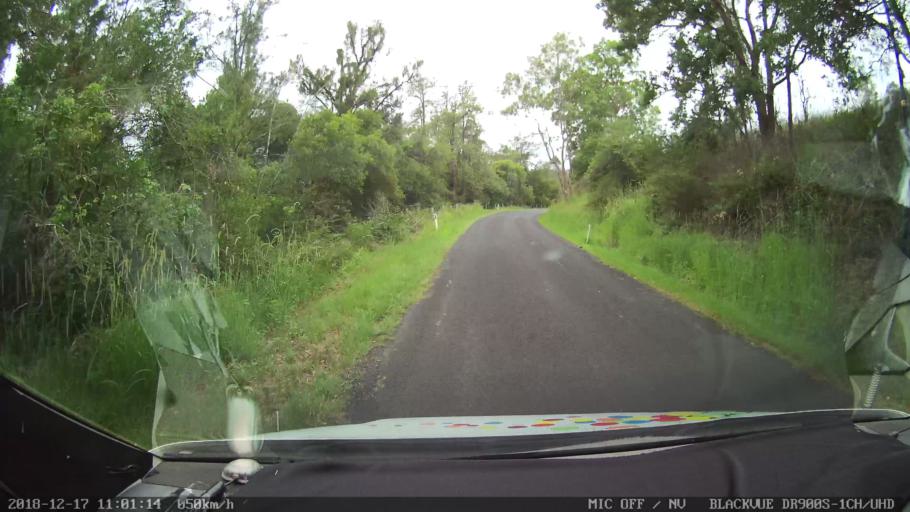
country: AU
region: New South Wales
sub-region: Richmond Valley
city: Casino
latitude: -28.8159
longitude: 152.6236
